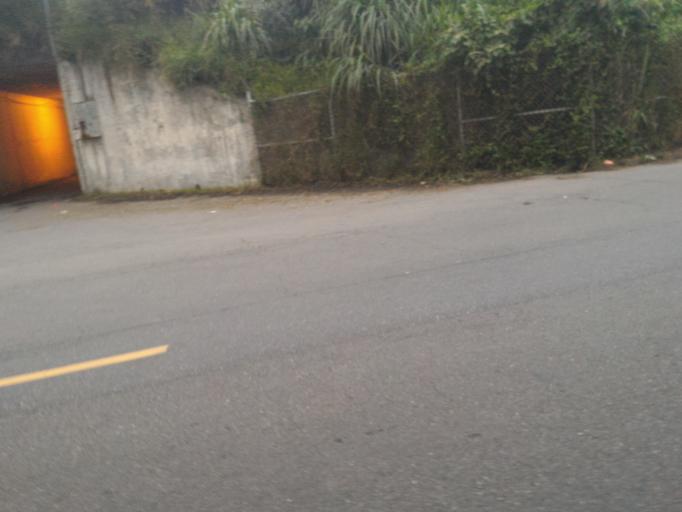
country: TW
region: Taiwan
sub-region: Taoyuan
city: Taoyuan
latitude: 24.9504
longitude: 121.4000
